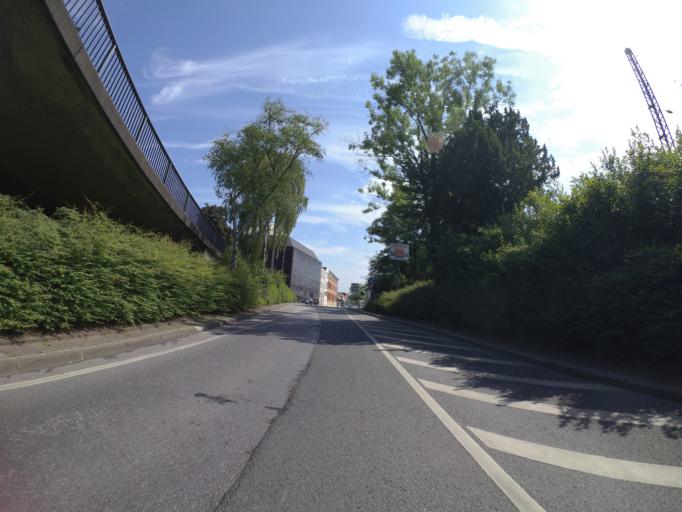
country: DE
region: North Rhine-Westphalia
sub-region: Regierungsbezirk Dusseldorf
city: Wuppertal
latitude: 51.2664
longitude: 7.1921
